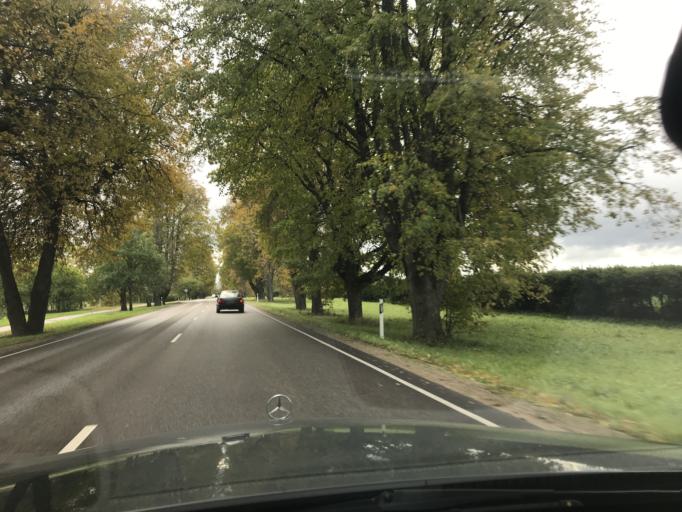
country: EE
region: Valgamaa
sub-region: Torva linn
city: Torva
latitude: 58.0131
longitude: 25.8859
